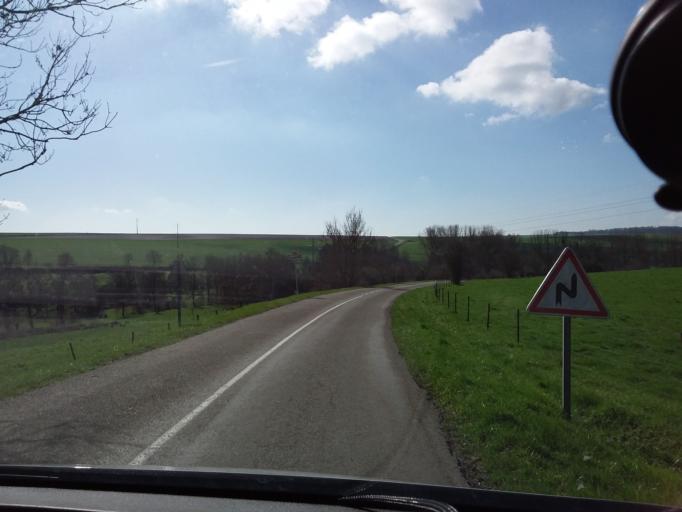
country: FR
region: Picardie
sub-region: Departement de l'Aisne
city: Origny-en-Thierache
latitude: 49.8012
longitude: 4.0093
